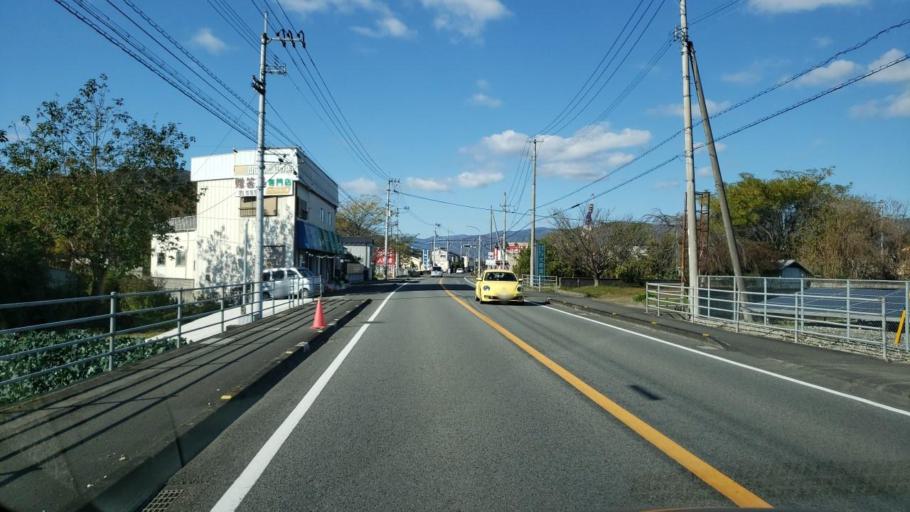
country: JP
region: Tokushima
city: Wakimachi
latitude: 34.0582
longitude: 134.2224
